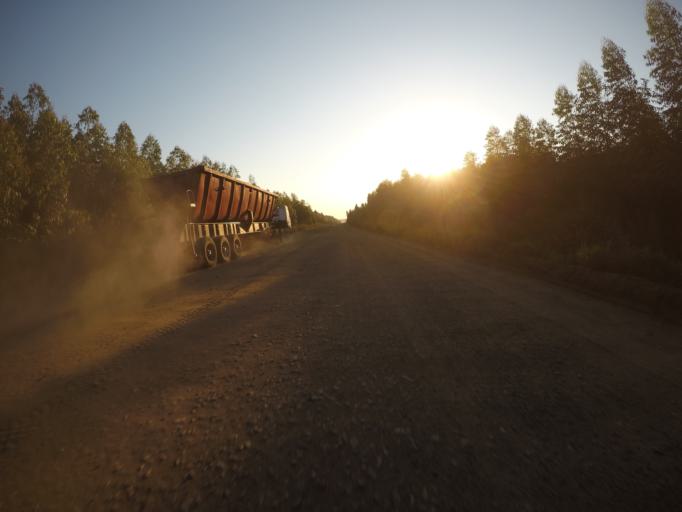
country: ZA
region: KwaZulu-Natal
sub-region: uThungulu District Municipality
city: KwaMbonambi
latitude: -28.6673
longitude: 32.0702
